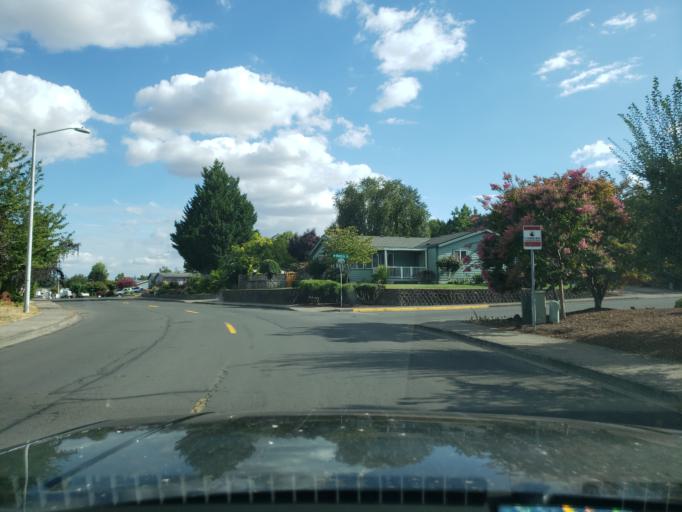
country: US
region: Oregon
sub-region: Yamhill County
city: McMinnville
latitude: 45.2158
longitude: -123.2204
